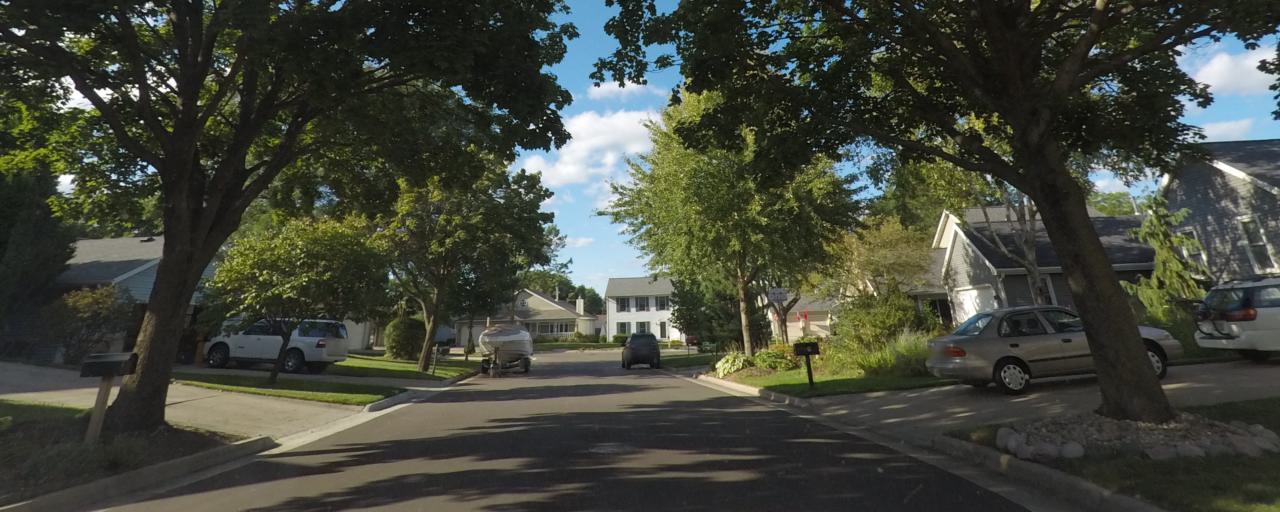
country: US
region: Wisconsin
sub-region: Dane County
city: Middleton
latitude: 43.0667
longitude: -89.5205
